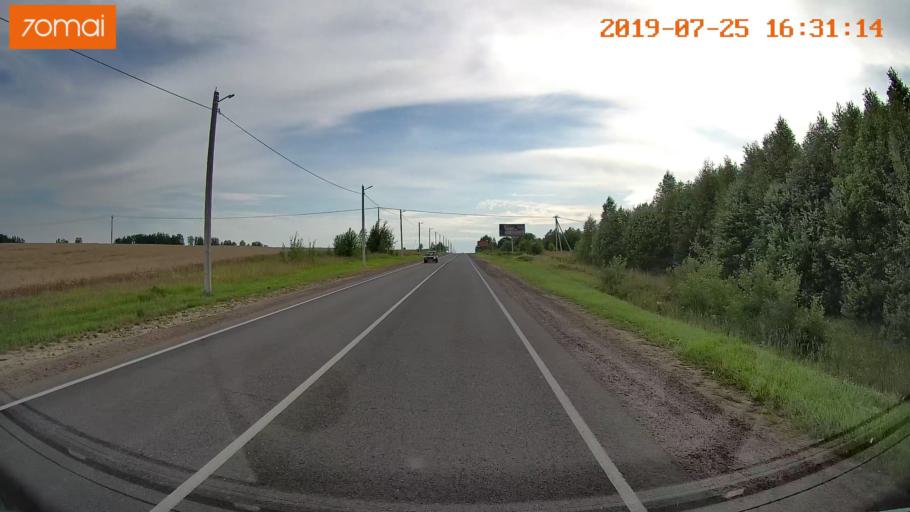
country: RU
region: Ivanovo
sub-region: Privolzhskiy Rayon
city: Ples
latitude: 57.4443
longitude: 41.4884
